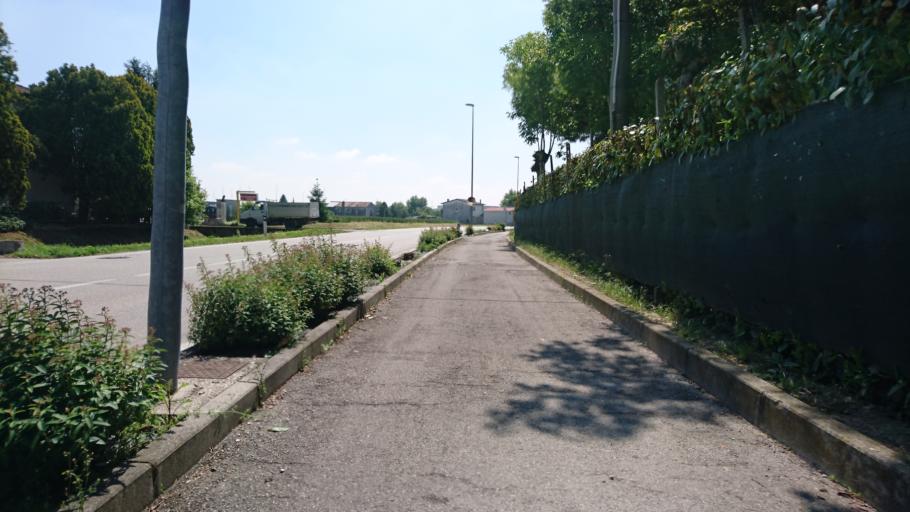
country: IT
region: Veneto
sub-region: Provincia di Padova
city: Casalserugo
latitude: 45.3146
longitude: 11.9090
